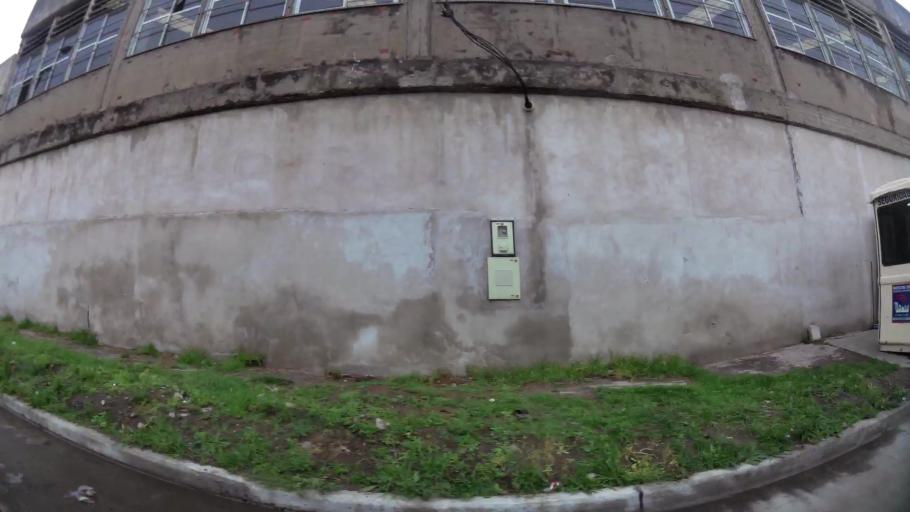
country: AR
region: Buenos Aires
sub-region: Partido de Lanus
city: Lanus
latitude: -34.7132
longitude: -58.3616
